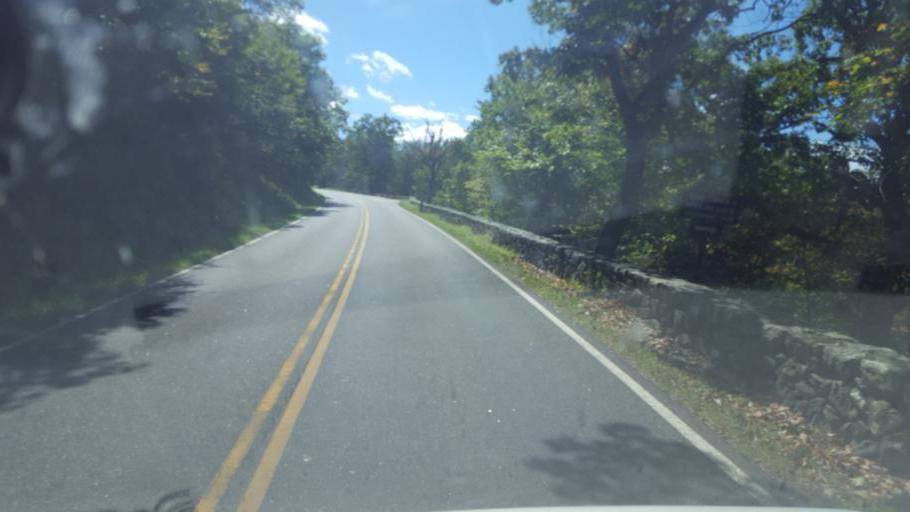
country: US
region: Virginia
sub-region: Greene County
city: Stanardsville
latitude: 38.4210
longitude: -78.4884
